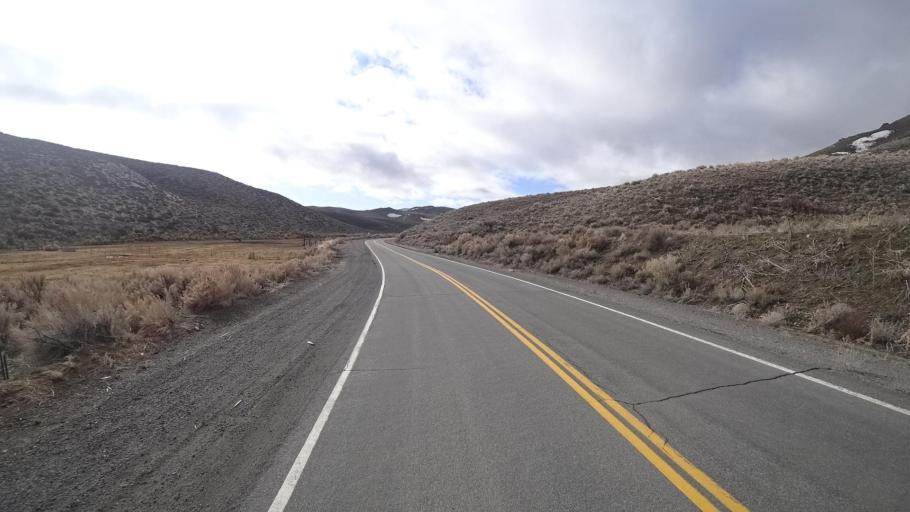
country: US
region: Nevada
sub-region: Washoe County
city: Cold Springs
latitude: 39.8114
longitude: -119.9335
